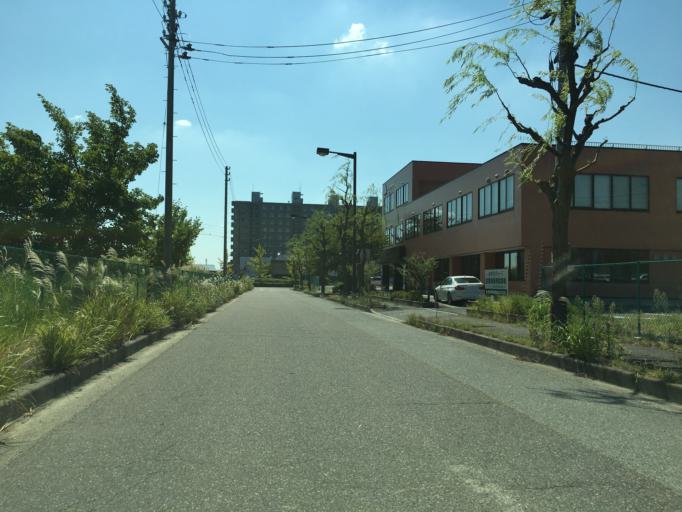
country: JP
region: Niigata
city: Niigata-shi
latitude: 37.8942
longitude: 139.0174
